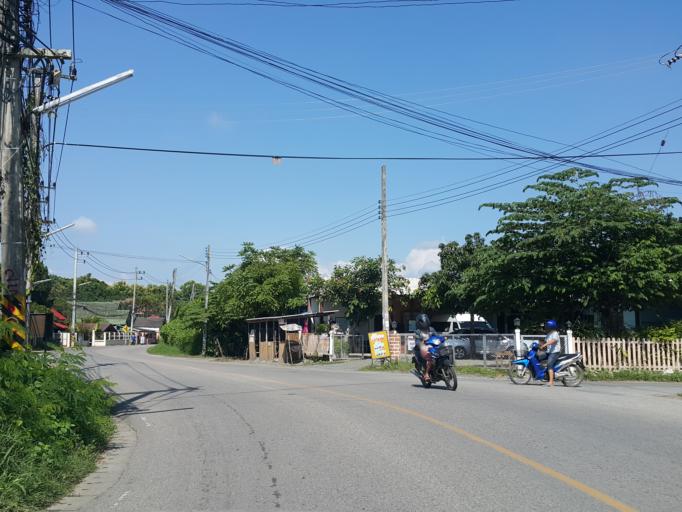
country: TH
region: Chiang Mai
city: San Kamphaeng
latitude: 18.7384
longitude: 99.1338
